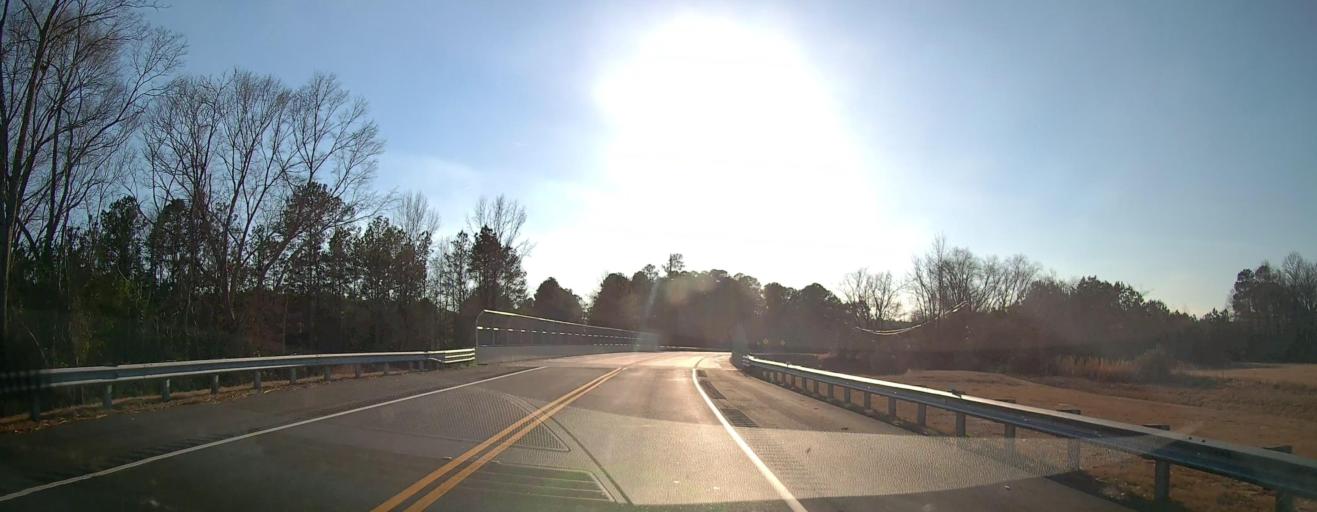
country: US
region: Georgia
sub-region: Harris County
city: Pine Mountain
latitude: 32.9169
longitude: -84.7745
